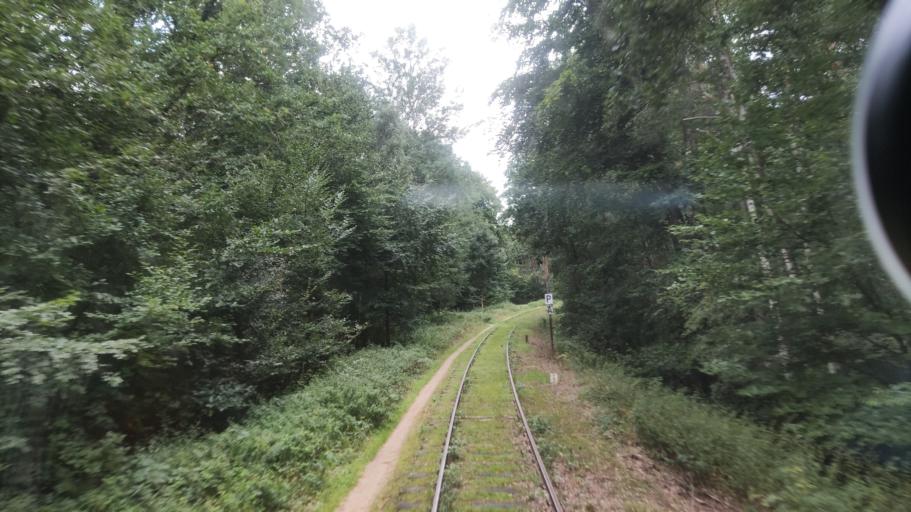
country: DE
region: Lower Saxony
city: Adendorf
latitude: 53.2576
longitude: 10.4492
